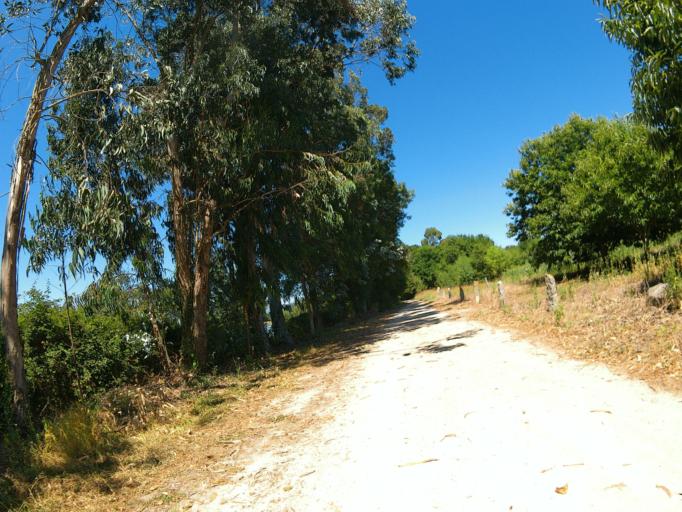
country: PT
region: Viana do Castelo
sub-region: Viana do Castelo
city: Darque
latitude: 41.7182
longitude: -8.6968
